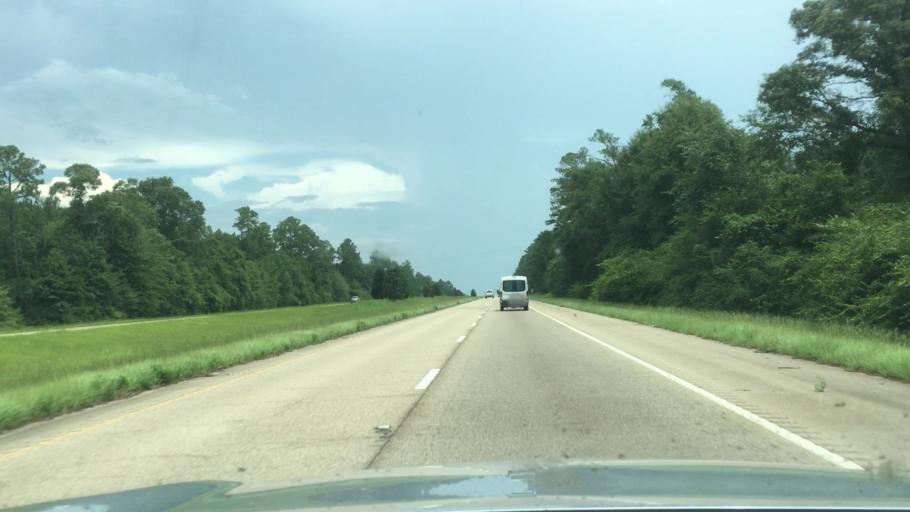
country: US
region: Mississippi
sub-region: Lamar County
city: Lumberton
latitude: 30.9529
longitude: -89.4430
